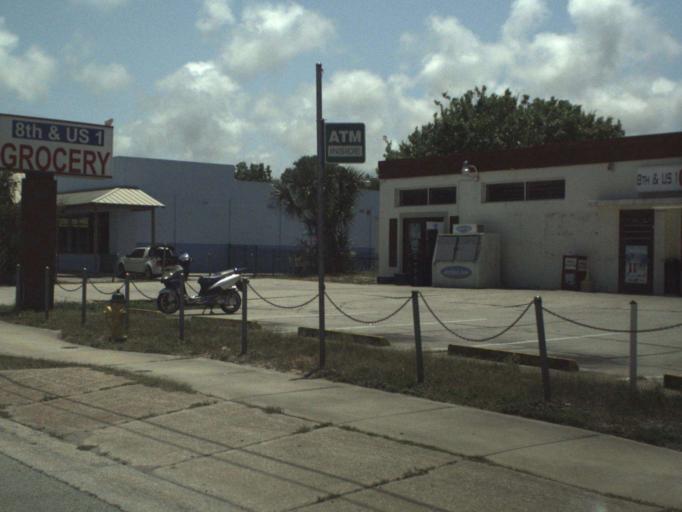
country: US
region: Florida
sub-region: Volusia County
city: Holly Hill
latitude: 29.2391
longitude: -81.0381
